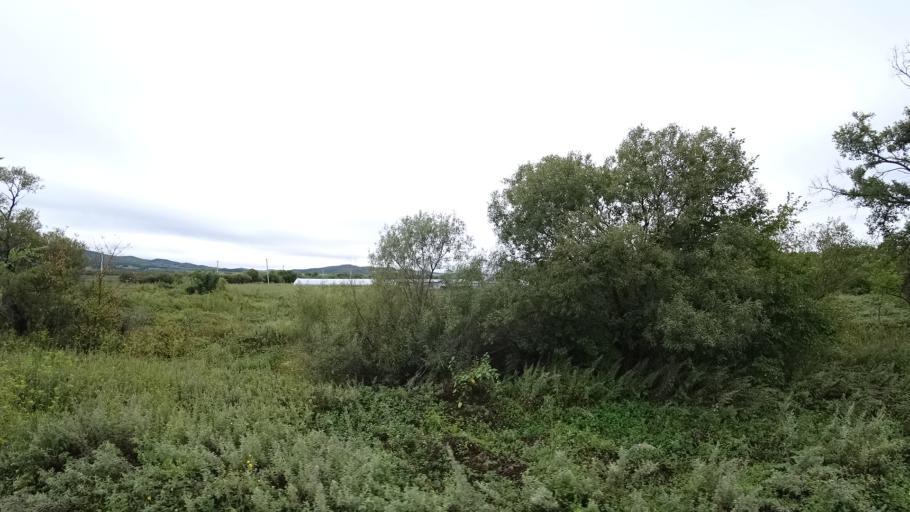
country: RU
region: Primorskiy
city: Monastyrishche
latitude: 44.1846
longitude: 132.4829
